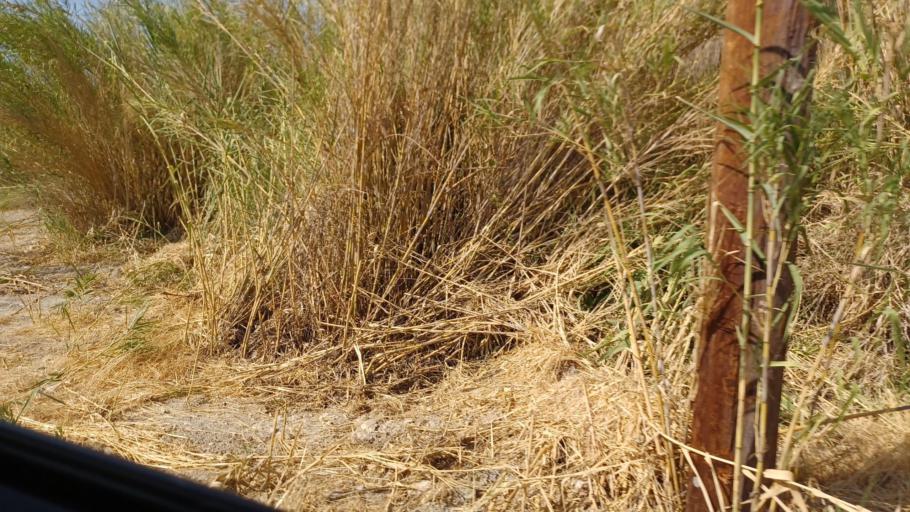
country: CY
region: Pafos
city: Tala
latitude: 34.9123
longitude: 32.4780
